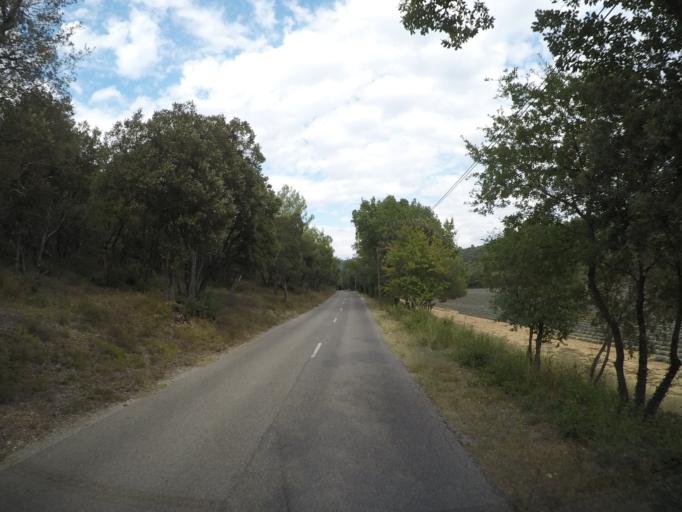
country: FR
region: Provence-Alpes-Cote d'Azur
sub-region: Departement des Alpes-de-Haute-Provence
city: Greoux-les-Bains
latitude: 43.7821
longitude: 5.9111
